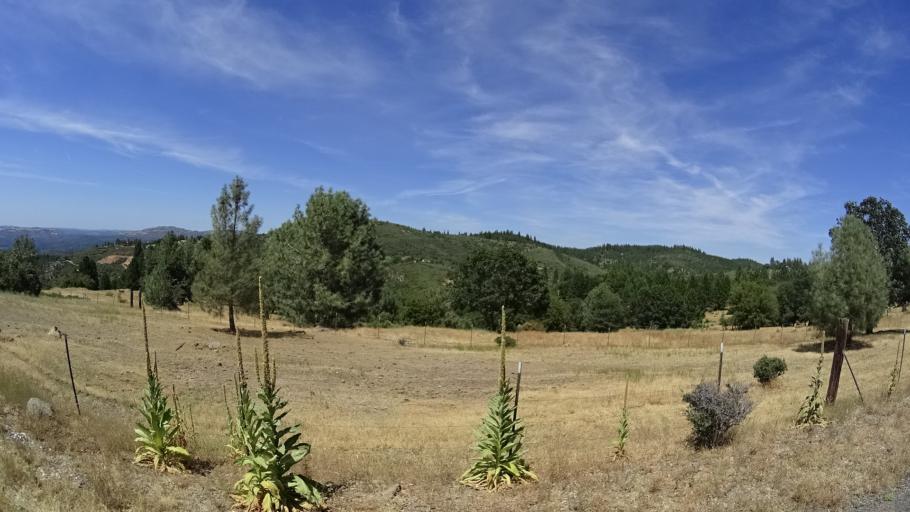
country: US
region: California
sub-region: Calaveras County
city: Forest Meadows
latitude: 38.1807
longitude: -120.4324
